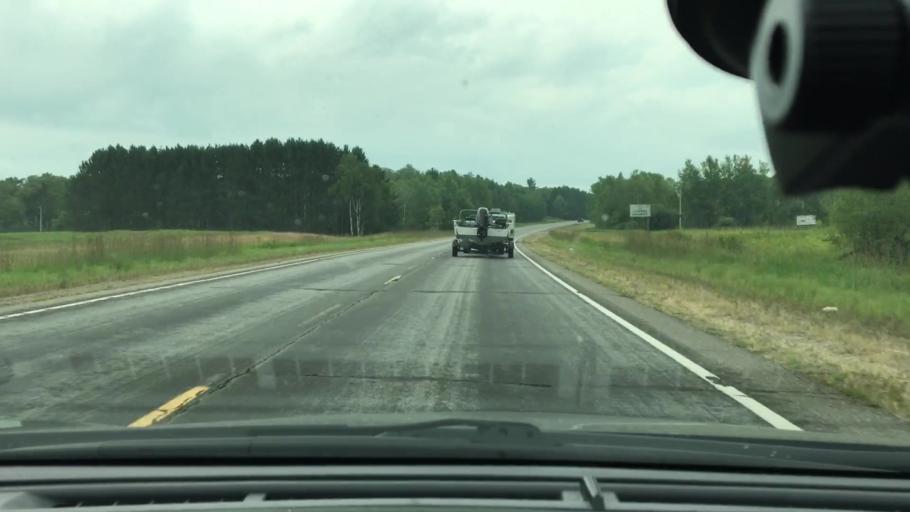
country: US
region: Minnesota
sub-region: Crow Wing County
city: Crosby
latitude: 46.6314
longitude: -93.9470
